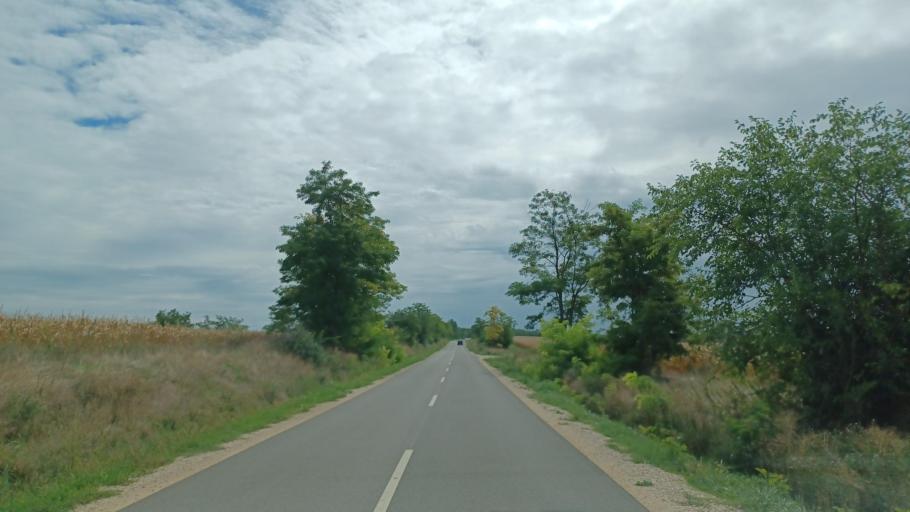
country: HU
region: Tolna
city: Zomba
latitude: 46.4484
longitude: 18.6046
